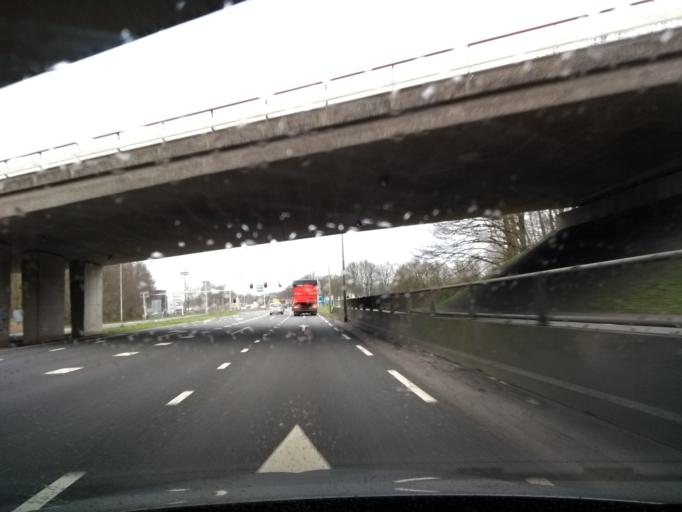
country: NL
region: Overijssel
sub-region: Gemeente Hengelo
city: Hengelo
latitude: 52.2381
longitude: 6.7627
